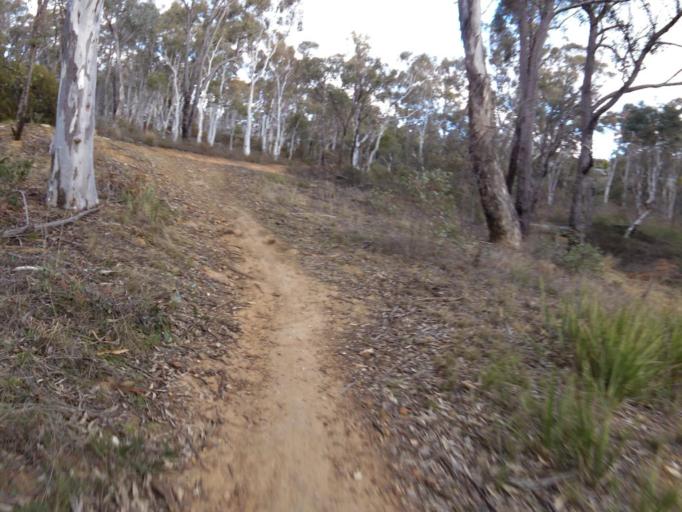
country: AU
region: Australian Capital Territory
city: Acton
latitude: -35.2600
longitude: 149.1093
